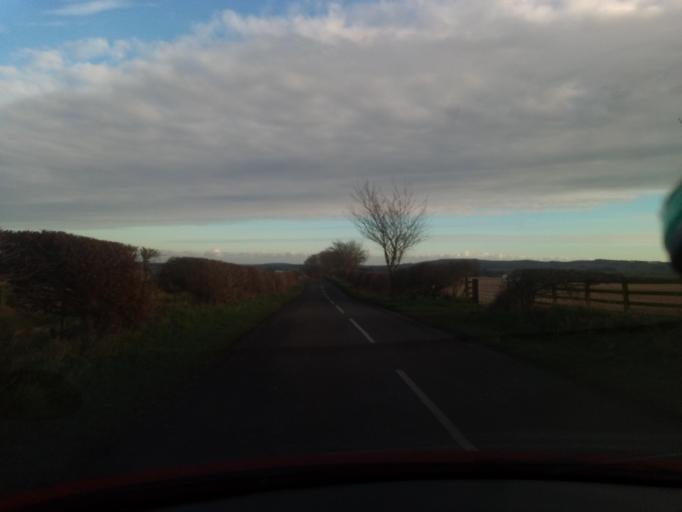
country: GB
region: Scotland
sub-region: The Scottish Borders
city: Chirnside
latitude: 55.8406
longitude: -2.1905
